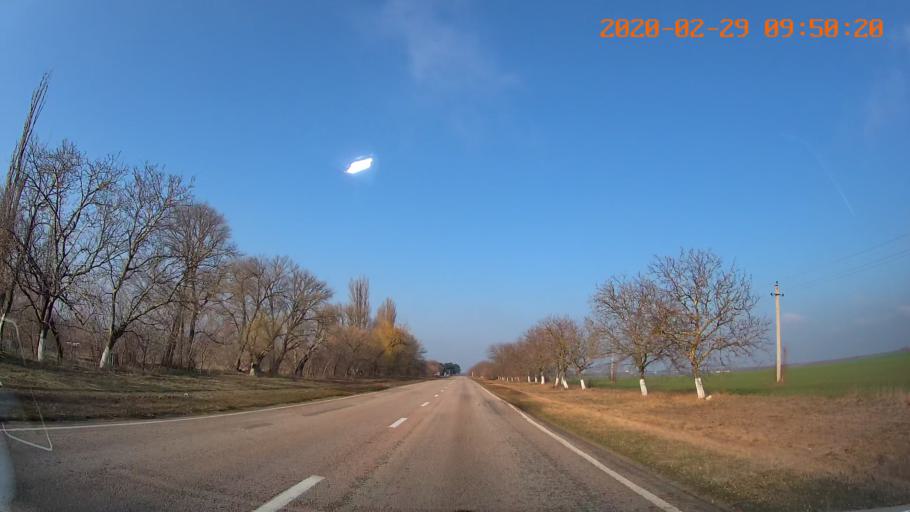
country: MD
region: Telenesti
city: Slobozia
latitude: 46.7019
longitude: 29.7574
